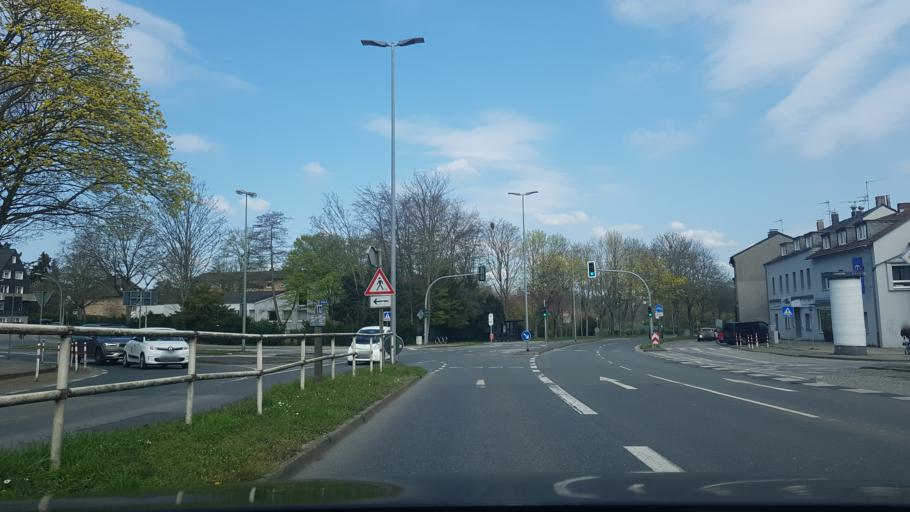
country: DE
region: North Rhine-Westphalia
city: Bochum-Hordel
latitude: 51.4683
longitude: 7.1459
